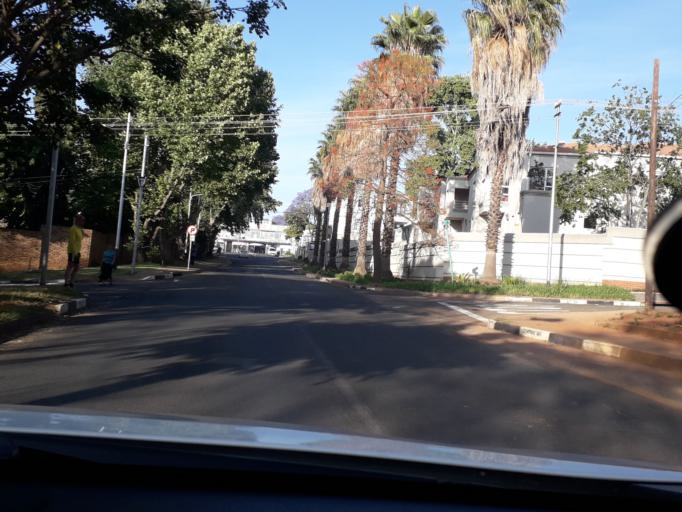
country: ZA
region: Gauteng
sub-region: City of Johannesburg Metropolitan Municipality
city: Johannesburg
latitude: -26.1267
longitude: 28.0514
